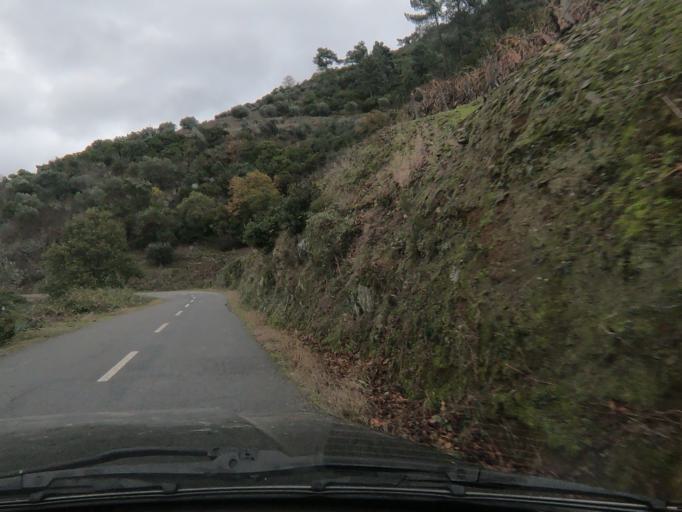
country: PT
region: Vila Real
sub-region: Santa Marta de Penaguiao
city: Santa Marta de Penaguiao
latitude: 41.2274
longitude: -7.7409
